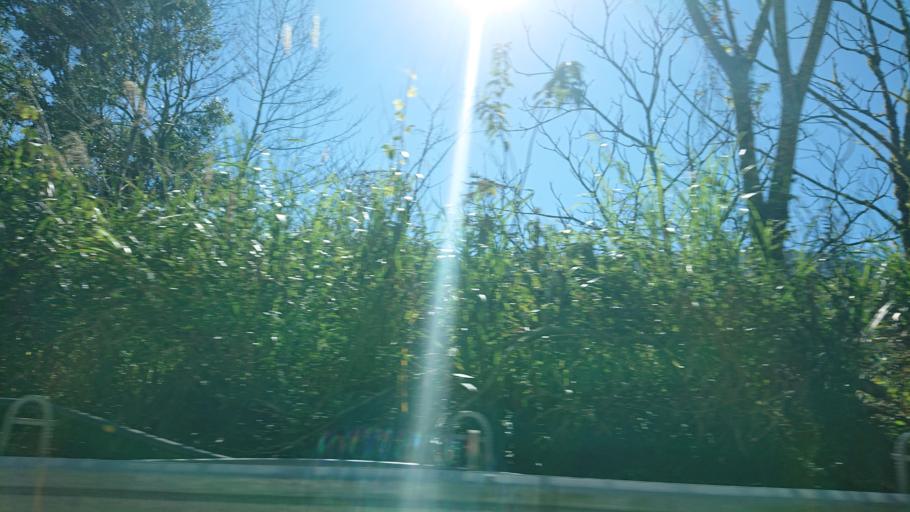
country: TW
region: Taiwan
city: Daxi
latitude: 24.4125
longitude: 121.3631
